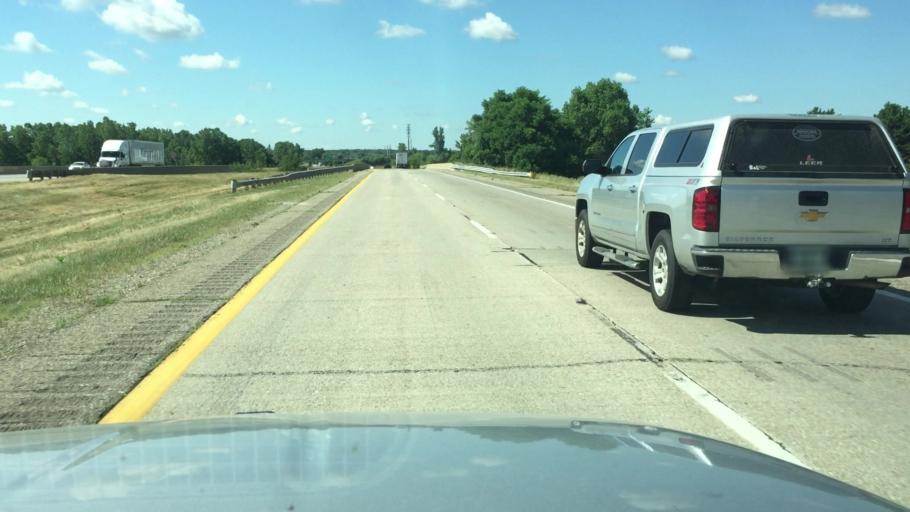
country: US
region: Michigan
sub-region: Eaton County
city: Charlotte
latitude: 42.5767
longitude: -84.8193
